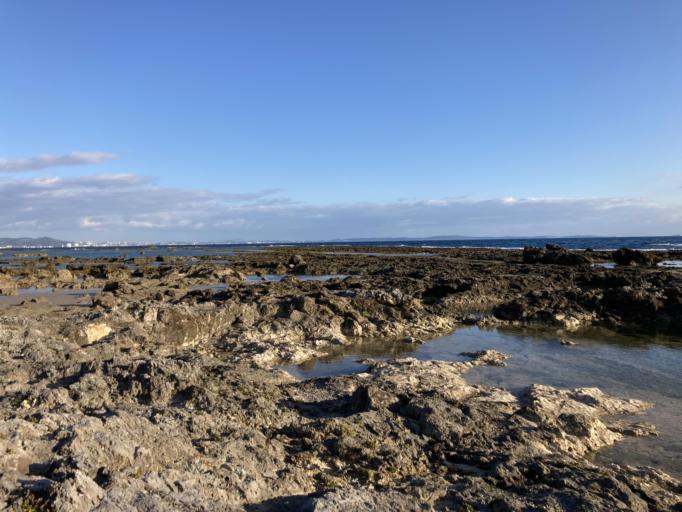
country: JP
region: Okinawa
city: Ginowan
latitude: 26.1883
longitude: 127.8227
